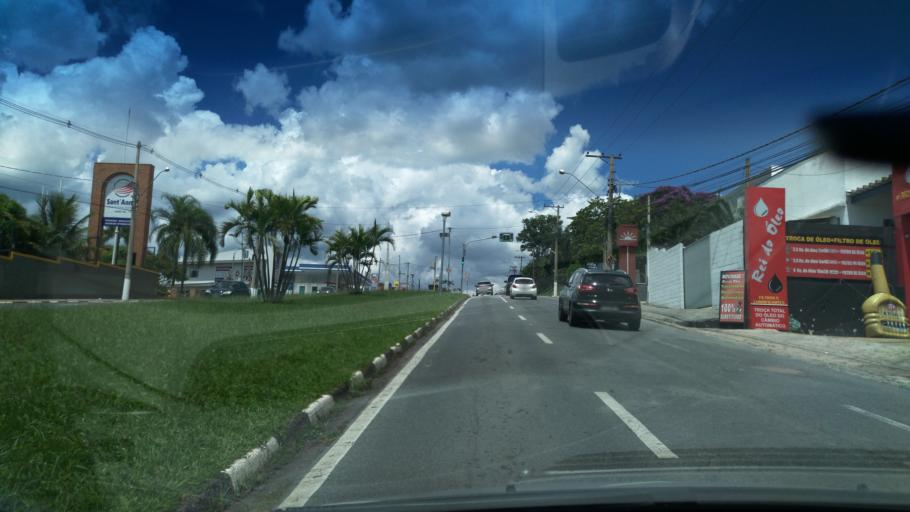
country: BR
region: Sao Paulo
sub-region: Vinhedo
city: Vinhedo
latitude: -23.0257
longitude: -46.9822
